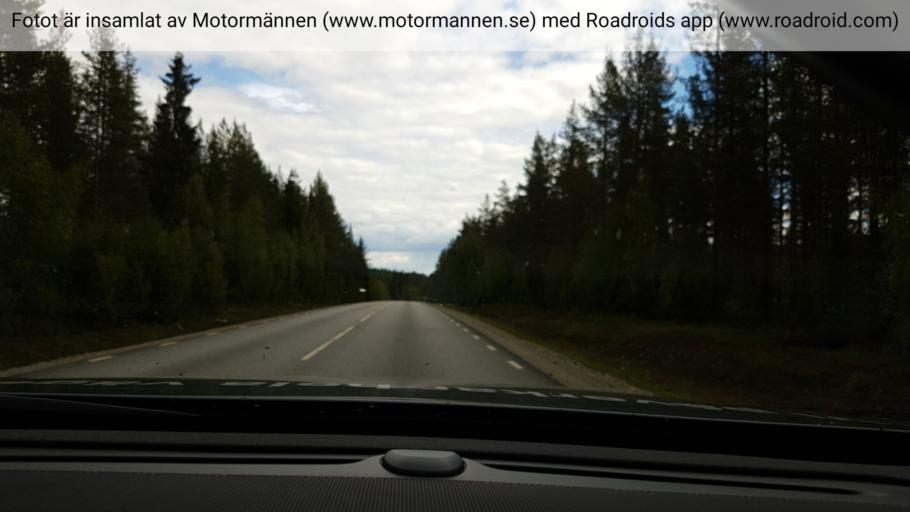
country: SE
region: Vaesterbotten
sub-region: Vindelns Kommun
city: Vindeln
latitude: 64.2086
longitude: 19.6577
